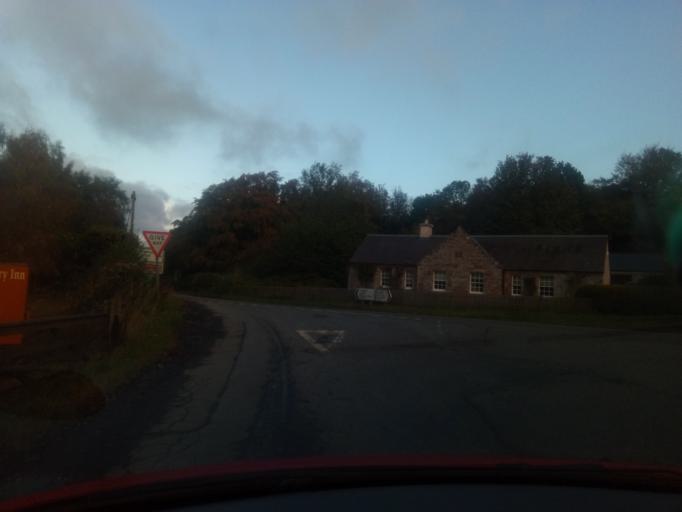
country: GB
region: Scotland
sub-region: The Scottish Borders
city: Jedburgh
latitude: 55.3883
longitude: -2.6436
